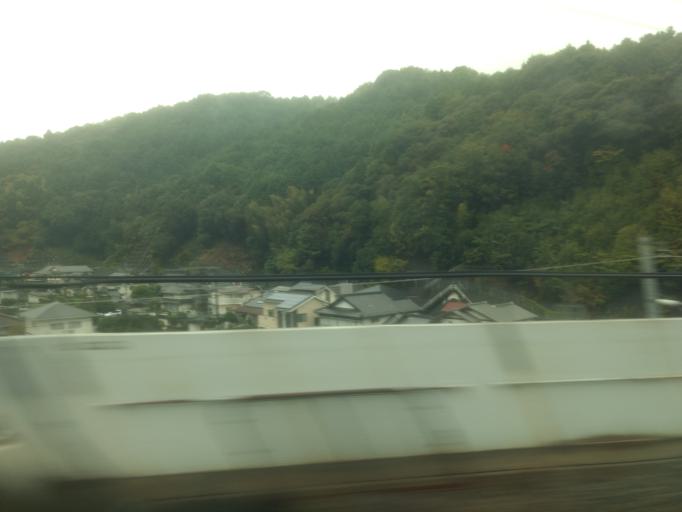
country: JP
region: Yamaguchi
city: Iwakuni
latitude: 34.1682
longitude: 132.1520
